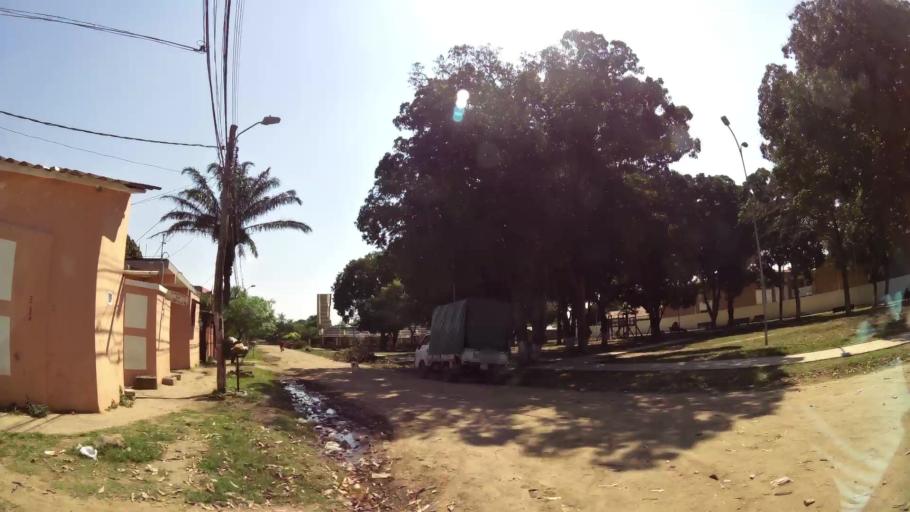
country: BO
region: Santa Cruz
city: Santa Cruz de la Sierra
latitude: -17.7294
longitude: -63.1617
